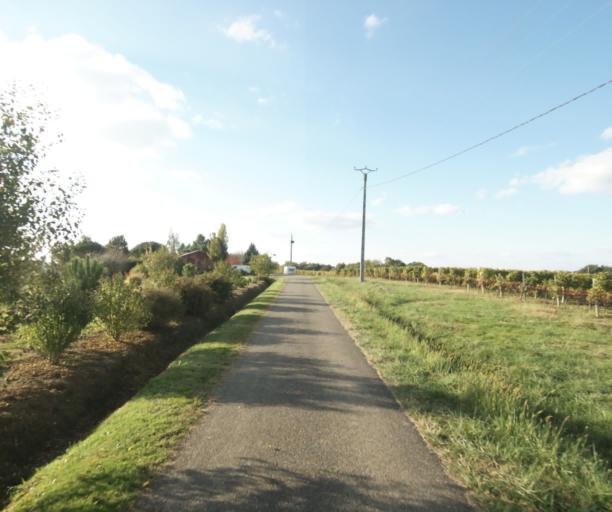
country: FR
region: Midi-Pyrenees
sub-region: Departement du Gers
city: Eauze
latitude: 43.7556
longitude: 0.0975
